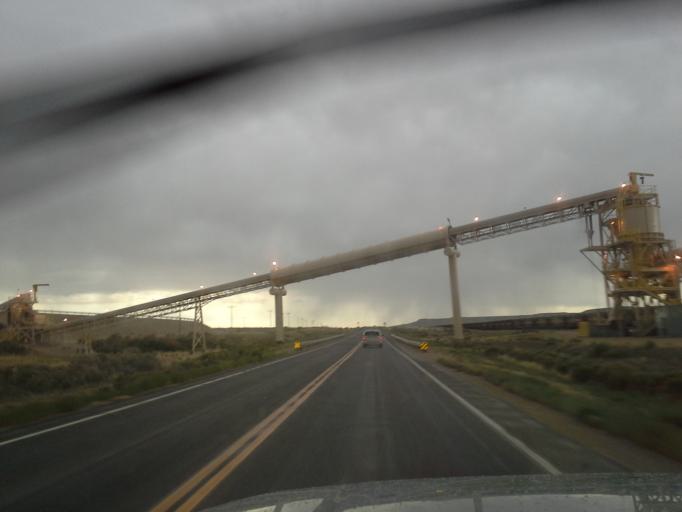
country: US
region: Wyoming
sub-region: Park County
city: Powell
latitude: 45.0569
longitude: -108.6570
